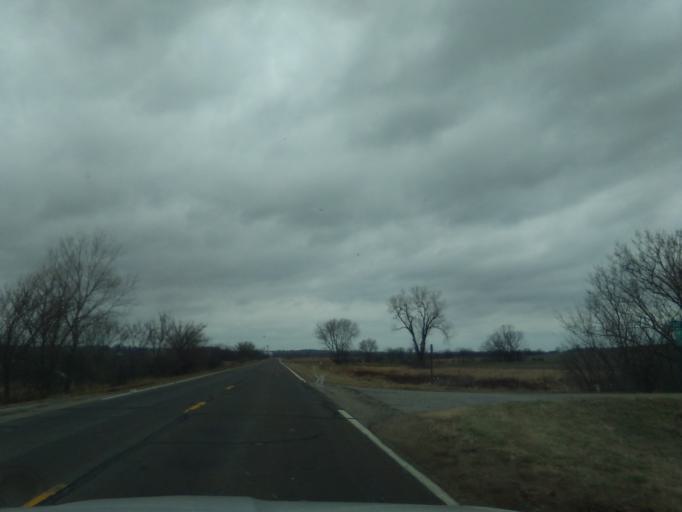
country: US
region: Nebraska
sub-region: Richardson County
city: Falls City
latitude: 40.0722
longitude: -95.6900
